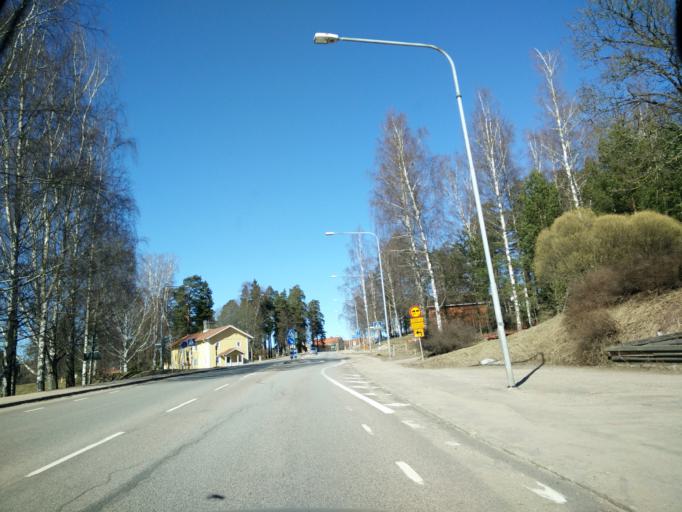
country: SE
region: Vaermland
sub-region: Hagfors Kommun
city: Hagfors
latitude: 60.0272
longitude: 13.6993
